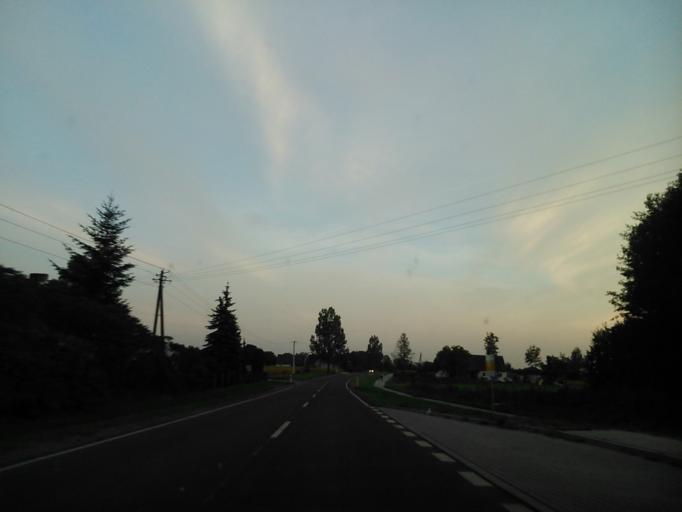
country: PL
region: Kujawsko-Pomorskie
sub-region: Powiat wabrzeski
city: Debowa Laka
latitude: 53.2142
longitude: 19.0323
